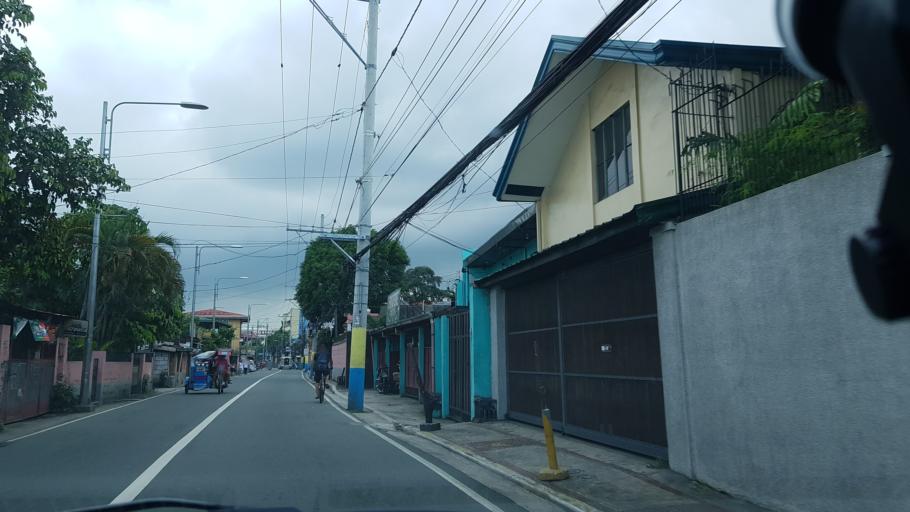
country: PH
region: Calabarzon
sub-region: Province of Rizal
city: Pateros
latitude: 14.5479
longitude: 121.0719
